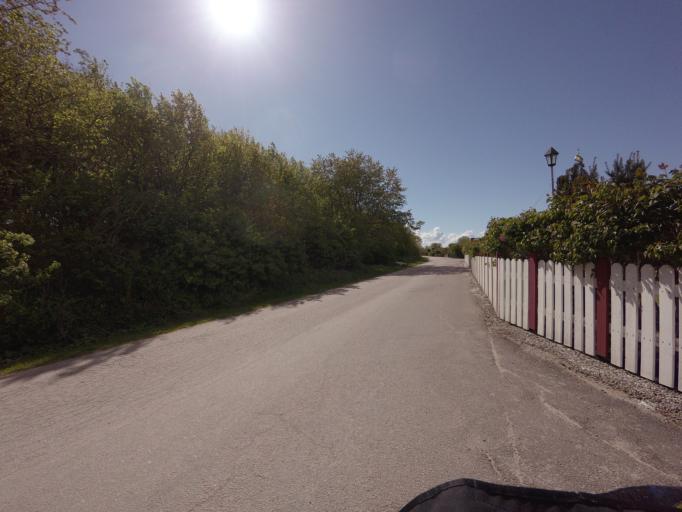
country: SE
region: Skane
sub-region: Landskrona
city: Landskrona
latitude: 55.8959
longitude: 12.8418
